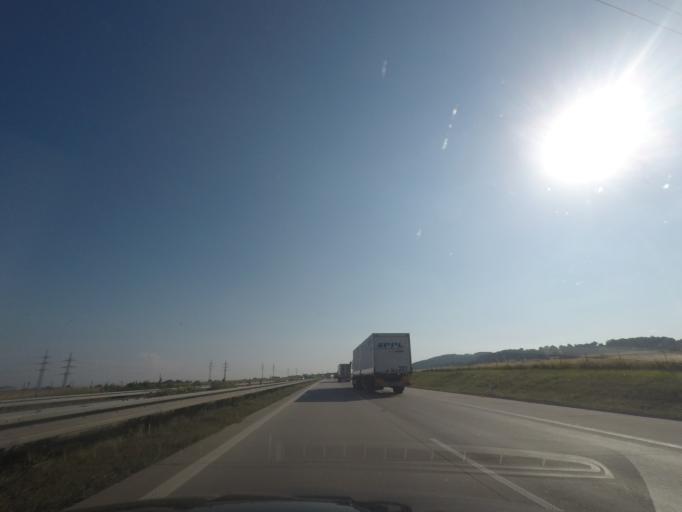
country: CZ
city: Fulnek
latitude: 49.6749
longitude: 17.9292
